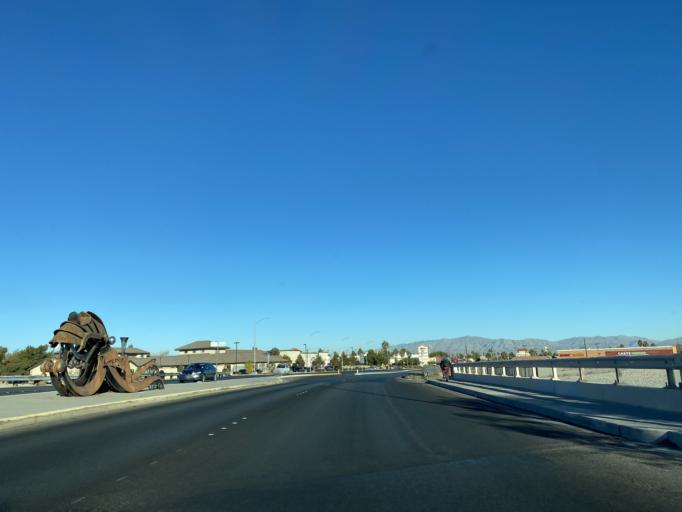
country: US
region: Nevada
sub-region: Clark County
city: Winchester
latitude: 36.1259
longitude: -115.1090
